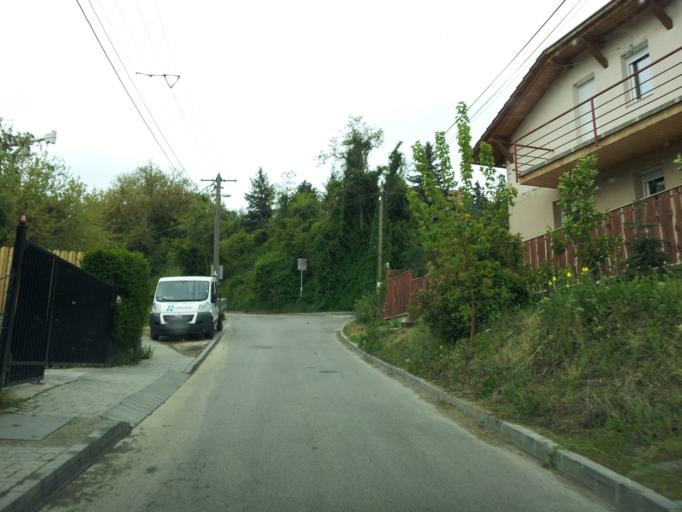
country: HU
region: Budapest
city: Budapest XXII. keruelet
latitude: 47.4395
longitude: 19.0215
